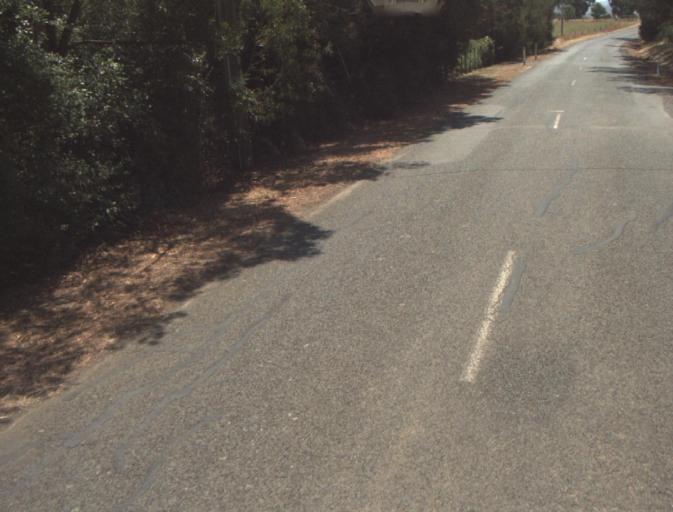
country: AU
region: Tasmania
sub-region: Northern Midlands
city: Perth
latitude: -41.5027
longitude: 147.2056
